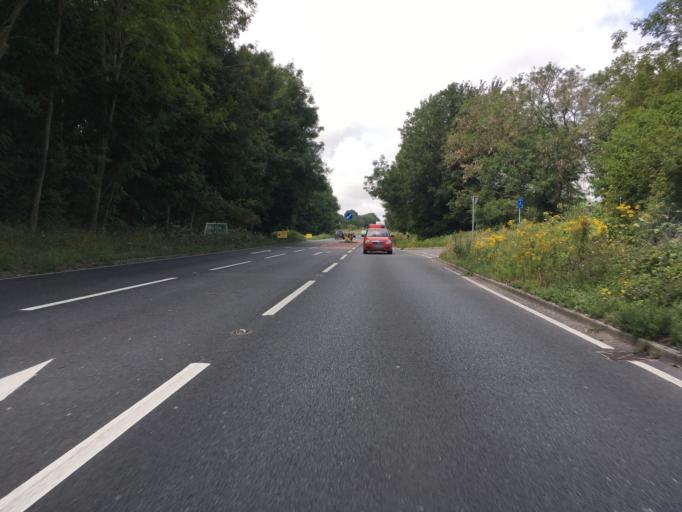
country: GB
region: England
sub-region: East Sussex
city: Ringmer
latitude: 50.8534
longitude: 0.0957
